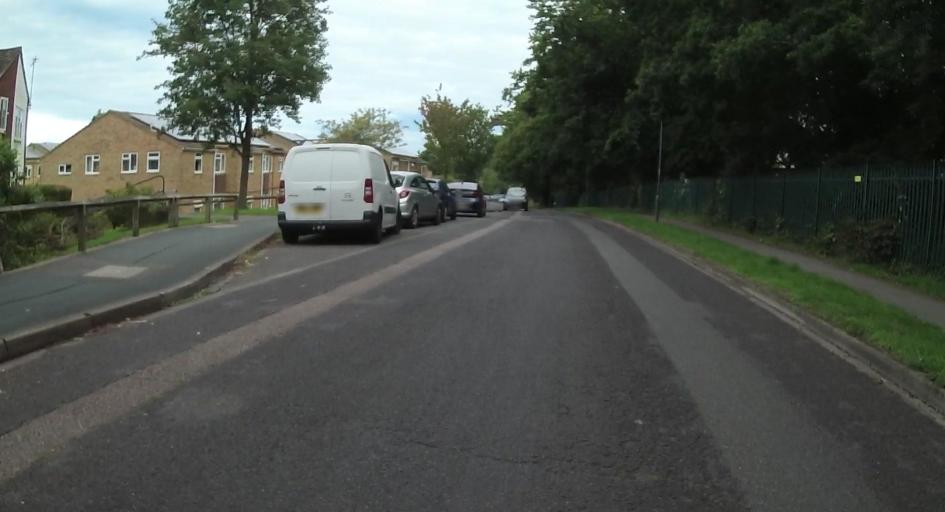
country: GB
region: England
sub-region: Surrey
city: Knaphill
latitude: 51.3142
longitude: -0.6031
